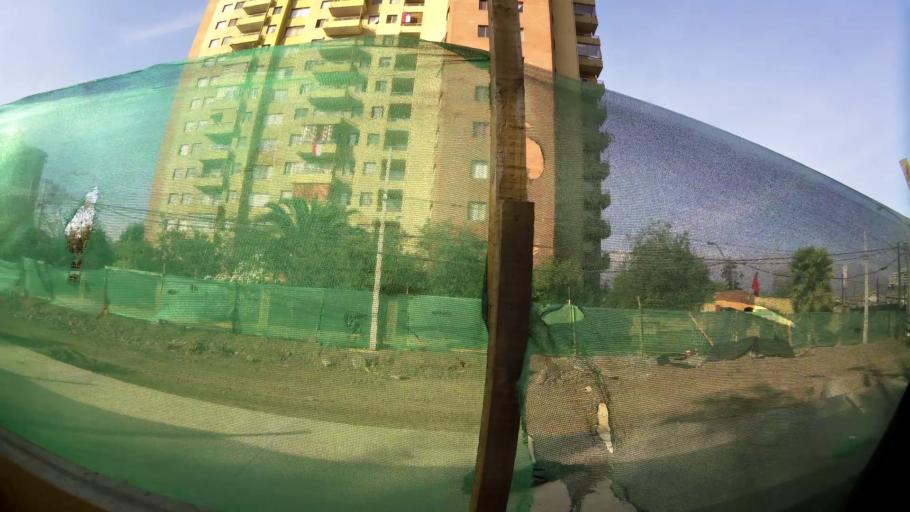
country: CL
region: Santiago Metropolitan
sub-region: Provincia de Santiago
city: Villa Presidente Frei, Nunoa, Santiago, Chile
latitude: -33.5127
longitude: -70.6094
